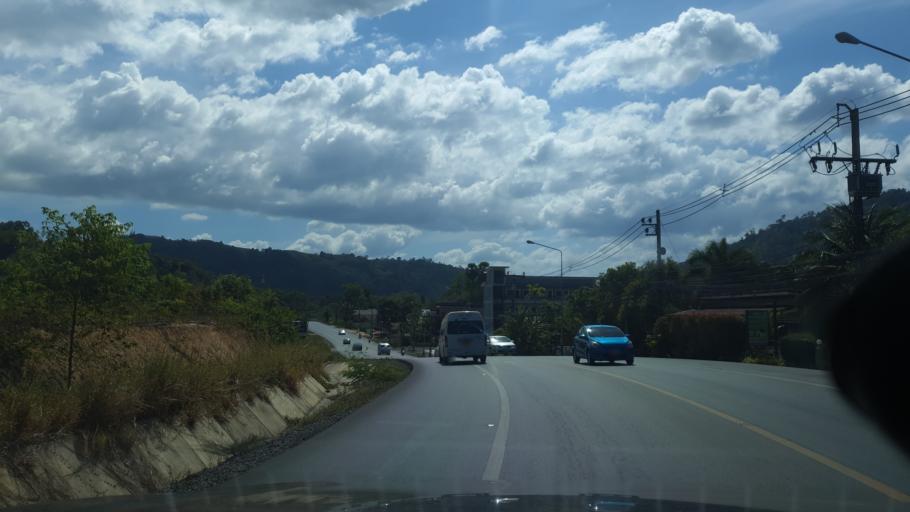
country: TH
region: Phuket
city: Thalang
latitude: 8.0827
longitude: 98.3023
